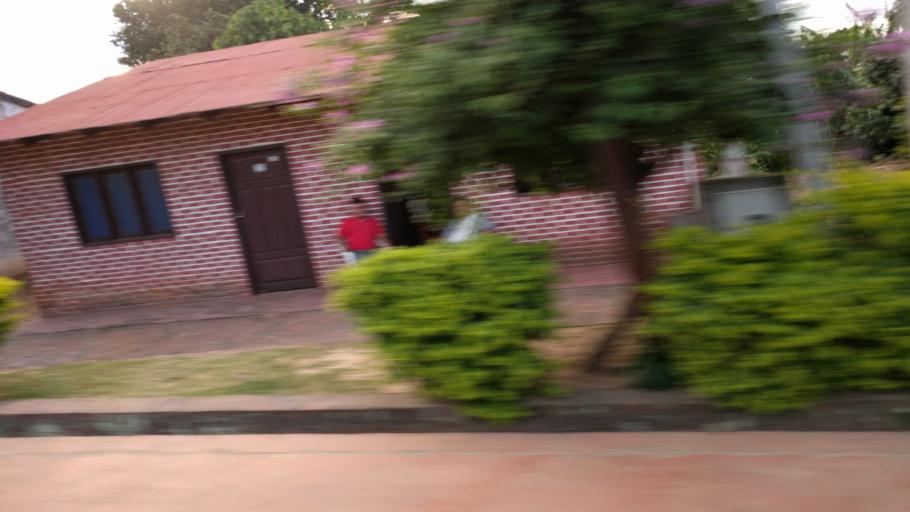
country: BO
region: Santa Cruz
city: Buena Vista
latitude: -17.4581
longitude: -63.6590
